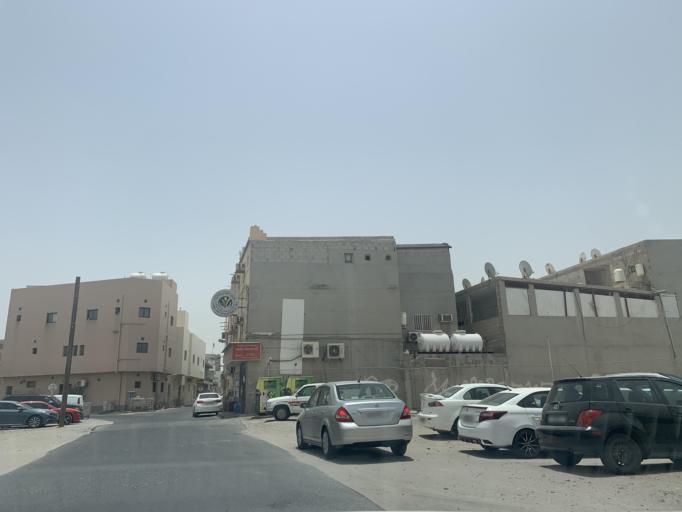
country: BH
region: Manama
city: Jidd Hafs
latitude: 26.2133
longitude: 50.5401
